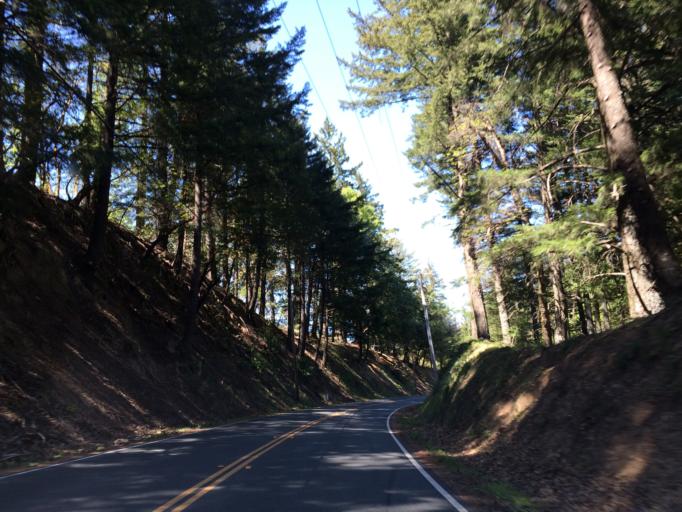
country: US
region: California
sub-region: Santa Clara County
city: Saratoga
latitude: 37.2118
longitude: -122.0671
